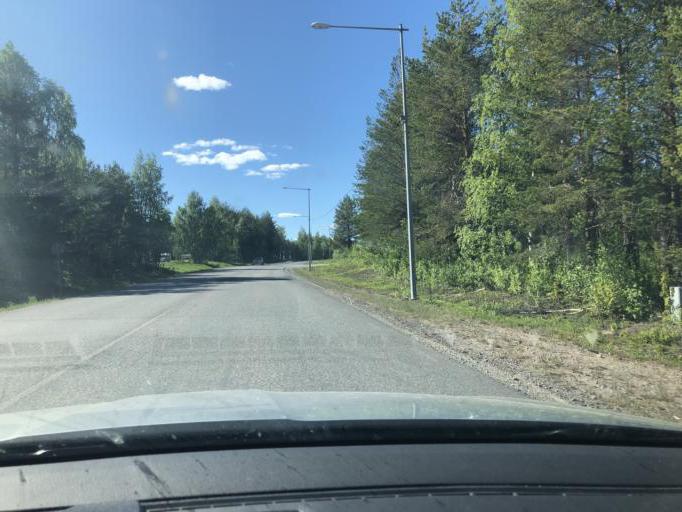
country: SE
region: Norrbotten
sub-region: Kalix Kommun
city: Kalix
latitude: 65.8593
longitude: 23.1623
